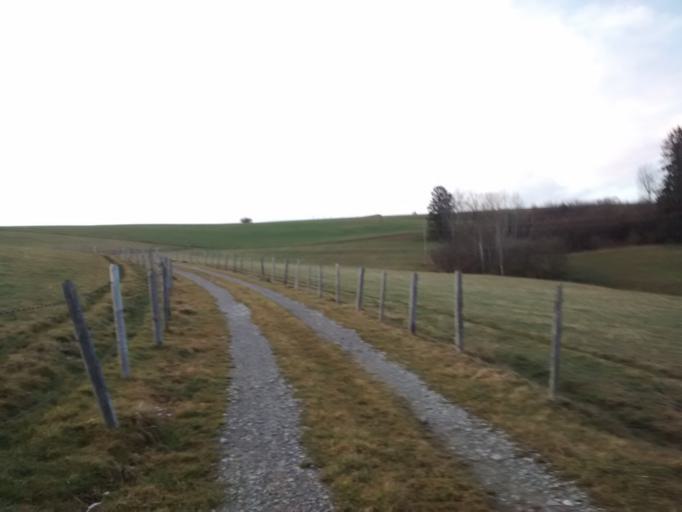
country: DE
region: Bavaria
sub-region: Swabia
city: Eggenthal
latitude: 47.8968
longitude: 10.4814
